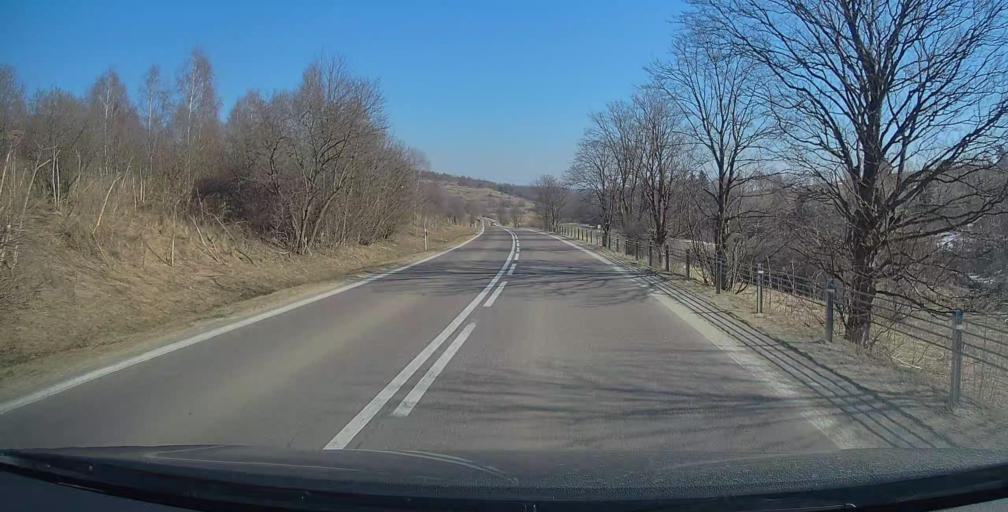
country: PL
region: Subcarpathian Voivodeship
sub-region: Powiat przemyski
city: Bircza
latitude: 49.5999
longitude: 22.4785
